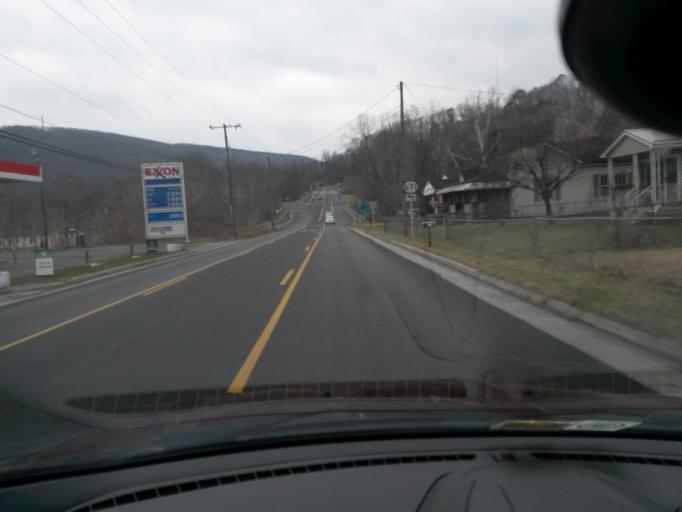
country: US
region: Virginia
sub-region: Alleghany County
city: Clifton Forge
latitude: 37.8219
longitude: -79.7975
